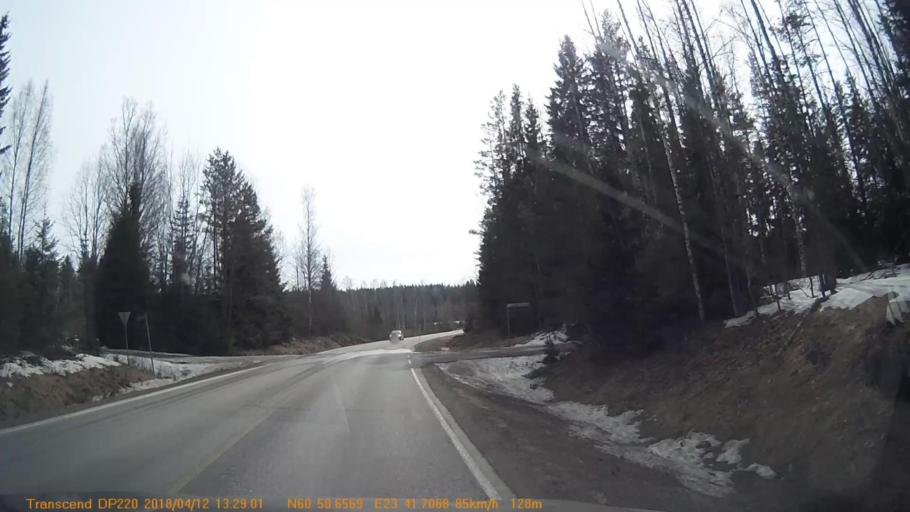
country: FI
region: Pirkanmaa
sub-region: Etelae-Pirkanmaa
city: Kylmaekoski
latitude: 60.9773
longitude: 23.6952
